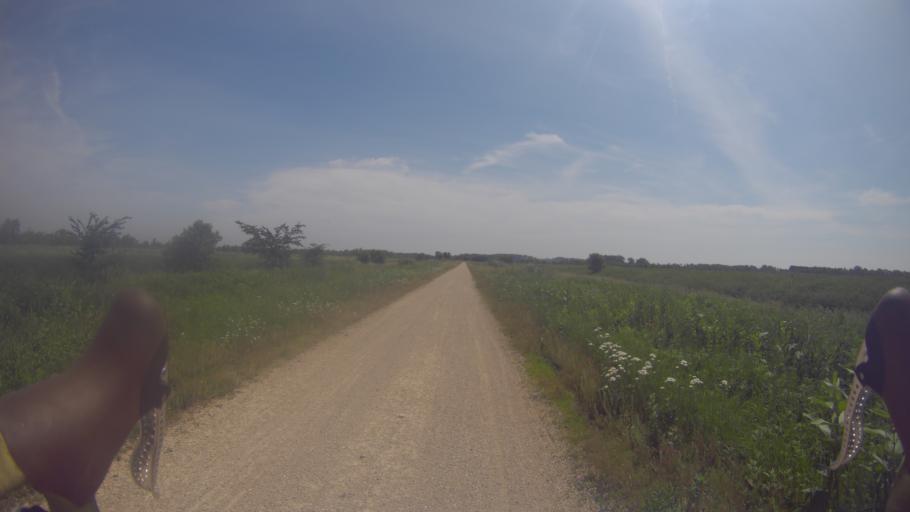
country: US
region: Wisconsin
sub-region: Jefferson County
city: Lake Ripley
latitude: 43.0570
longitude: -88.9827
